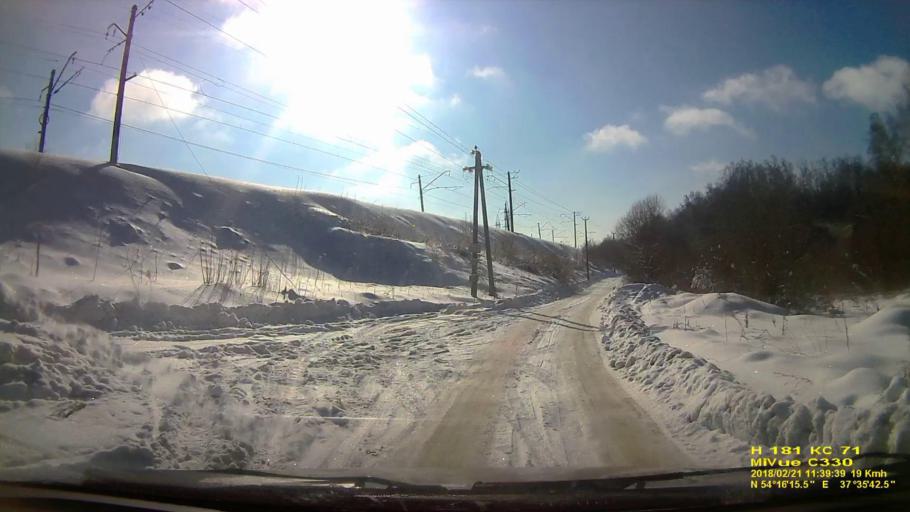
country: RU
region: Tula
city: Gorelki
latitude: 54.2709
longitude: 37.5951
